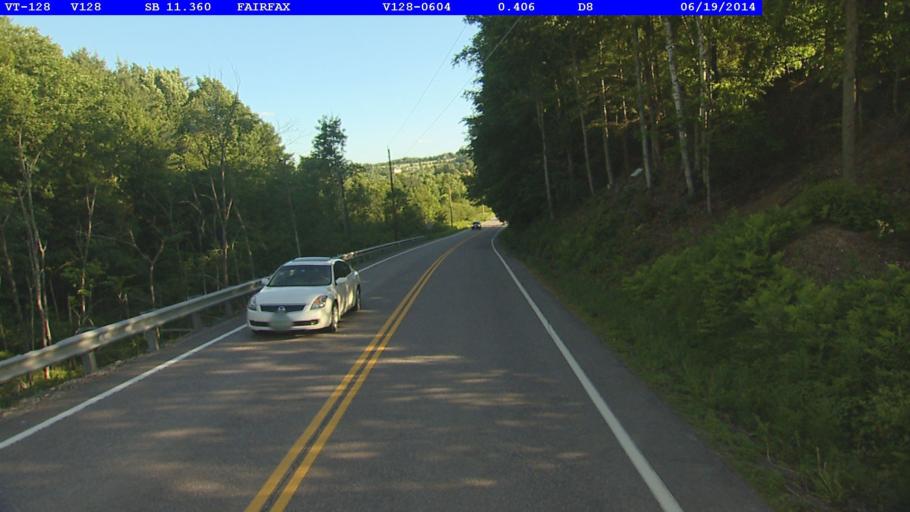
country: US
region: Vermont
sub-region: Chittenden County
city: Milton
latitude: 44.6523
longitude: -73.0105
